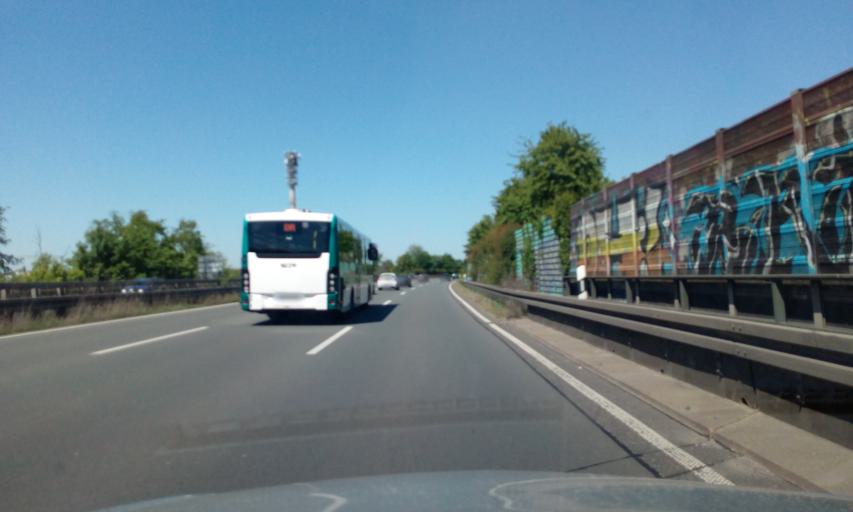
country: DE
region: North Rhine-Westphalia
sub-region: Regierungsbezirk Koln
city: Bonn
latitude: 50.7384
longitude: 7.1460
